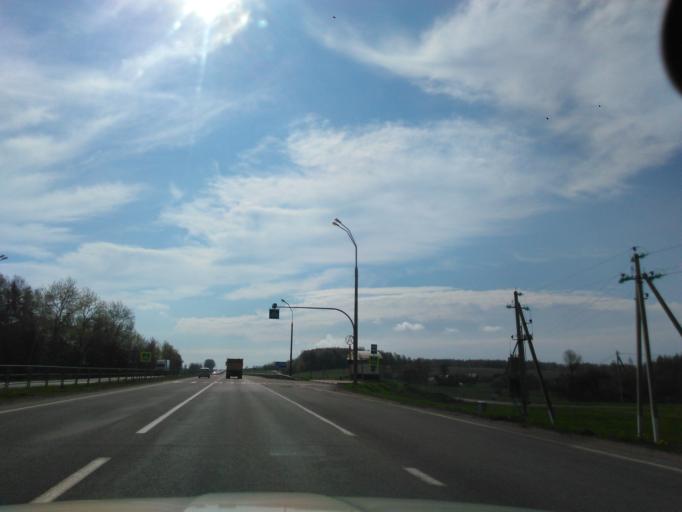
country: BY
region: Minsk
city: Novosel'ye
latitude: 53.9292
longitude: 27.1529
